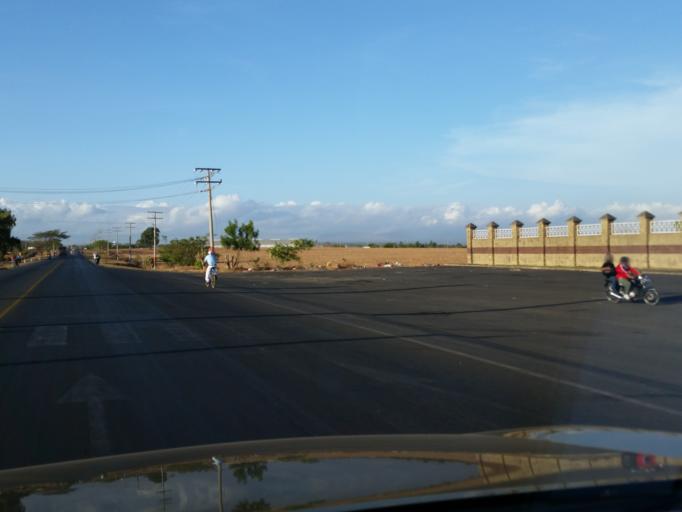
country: NI
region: Managua
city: Tipitapa
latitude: 12.1642
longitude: -86.0930
